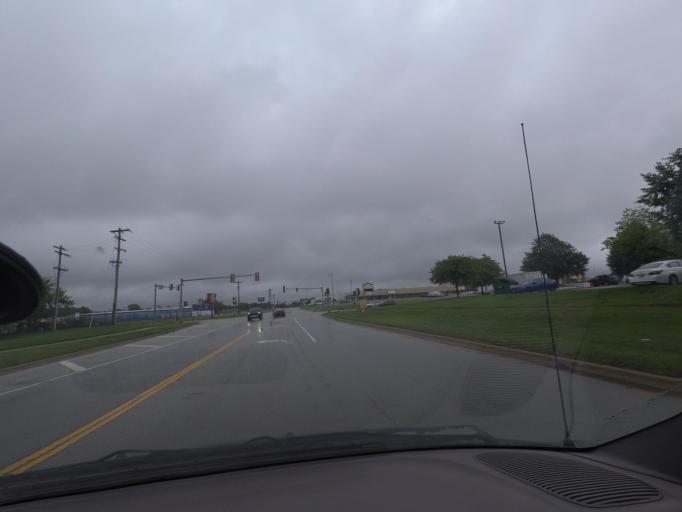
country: US
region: Illinois
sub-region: Champaign County
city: Champaign
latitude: 40.1179
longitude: -88.2817
